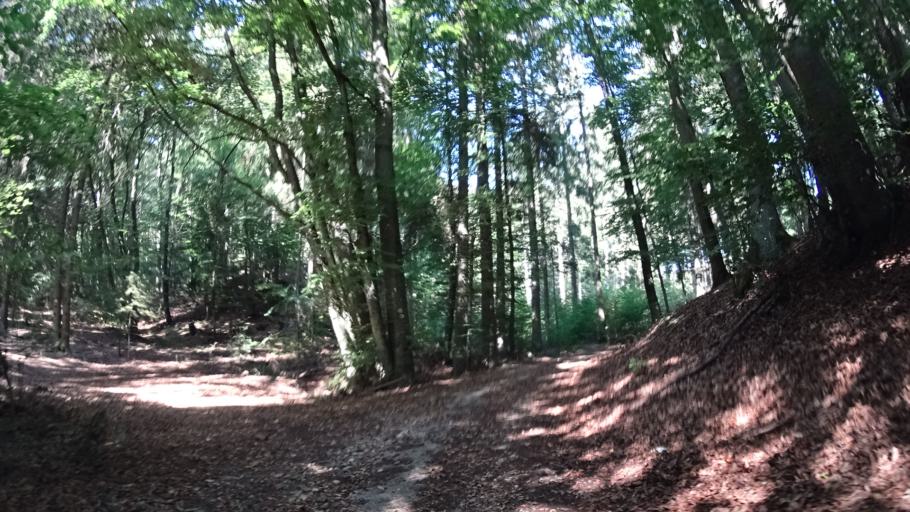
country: DE
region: Bavaria
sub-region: Upper Bavaria
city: Walting
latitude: 48.9500
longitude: 11.3547
